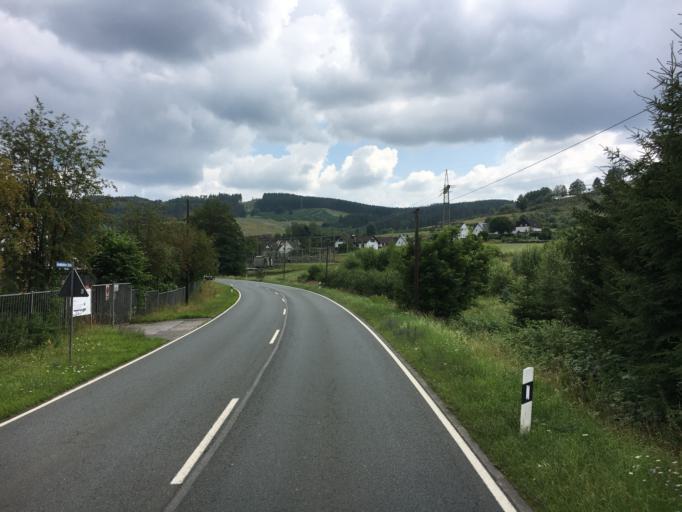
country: DE
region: North Rhine-Westphalia
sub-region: Regierungsbezirk Arnsberg
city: Lennestadt
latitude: 51.1237
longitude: 8.0386
